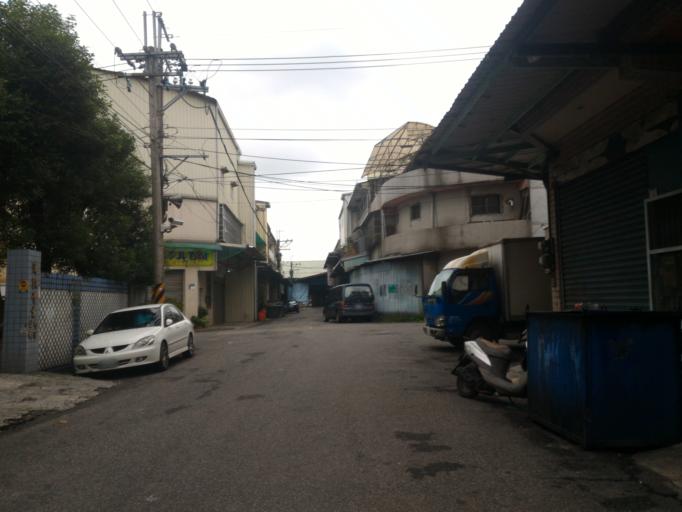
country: TW
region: Taiwan
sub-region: Taoyuan
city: Taoyuan
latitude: 24.9634
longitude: 121.3937
